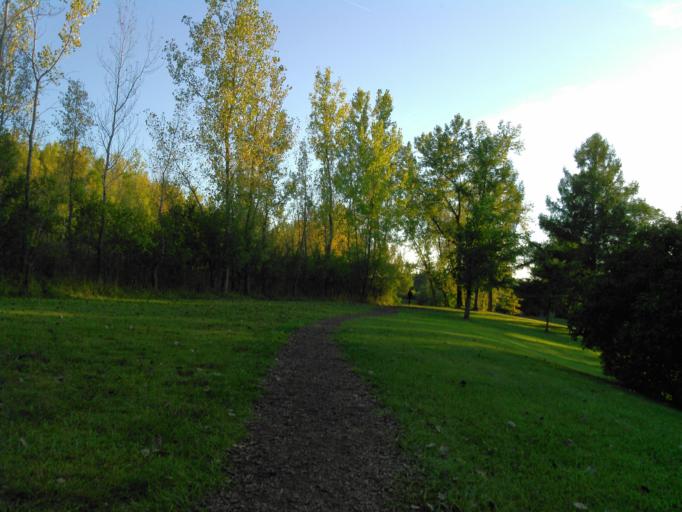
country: US
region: New York
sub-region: Onondaga County
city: Syracuse
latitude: 43.0262
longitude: -76.1155
